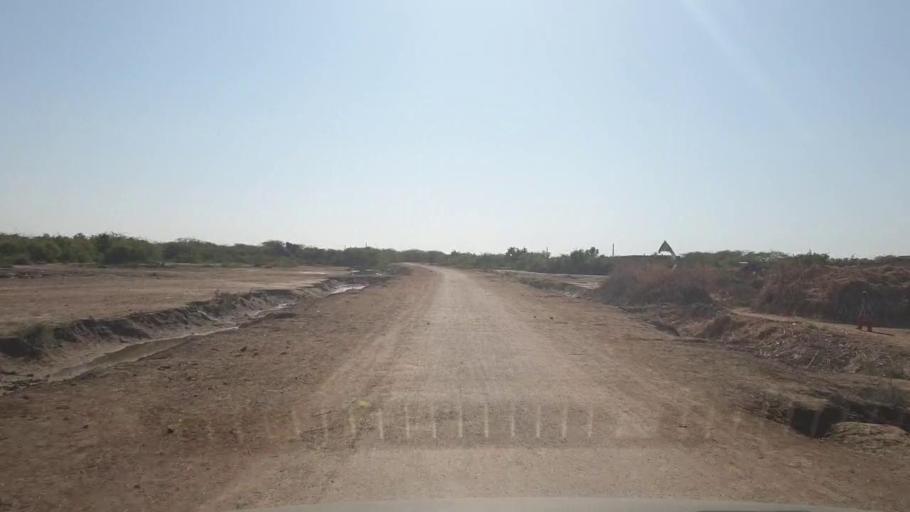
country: PK
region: Sindh
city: Dhoro Naro
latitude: 25.4086
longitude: 69.5895
